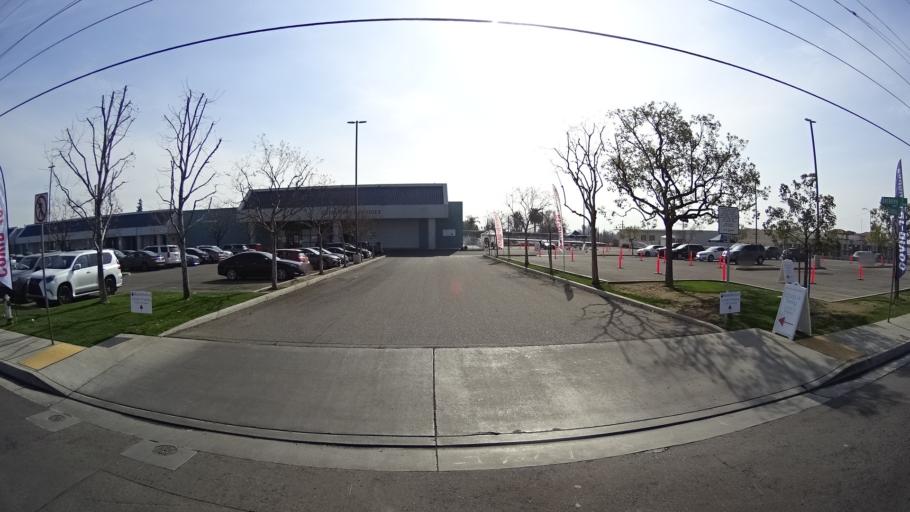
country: US
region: California
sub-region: Kern County
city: Oildale
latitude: 35.3974
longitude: -118.9830
